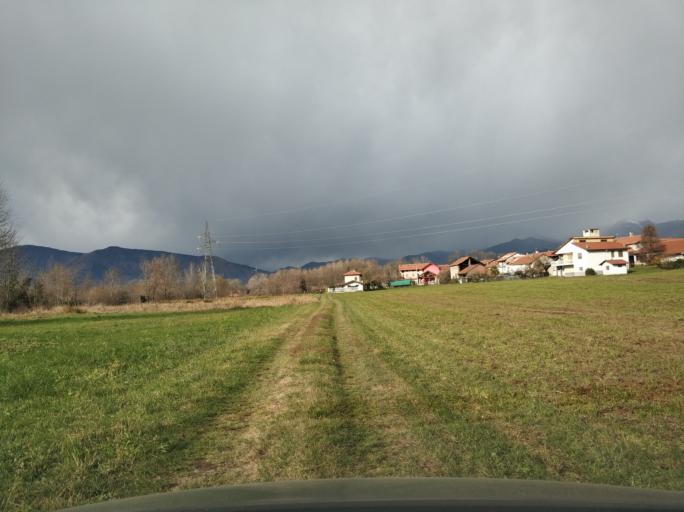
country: IT
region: Piedmont
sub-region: Provincia di Torino
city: Cirie
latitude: 45.2217
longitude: 7.5844
